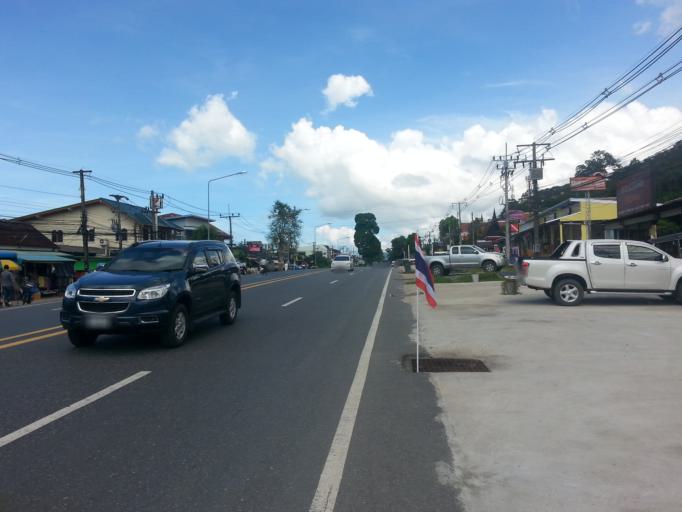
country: TH
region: Phangnga
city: Ban Khao Lak
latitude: 8.6466
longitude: 98.2520
